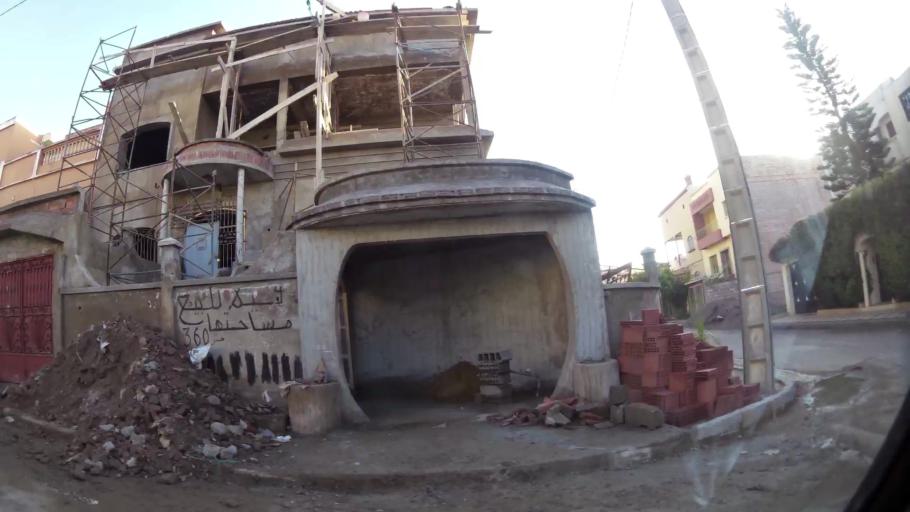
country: MA
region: Chaouia-Ouardigha
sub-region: Settat Province
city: Settat
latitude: 33.0100
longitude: -7.6036
